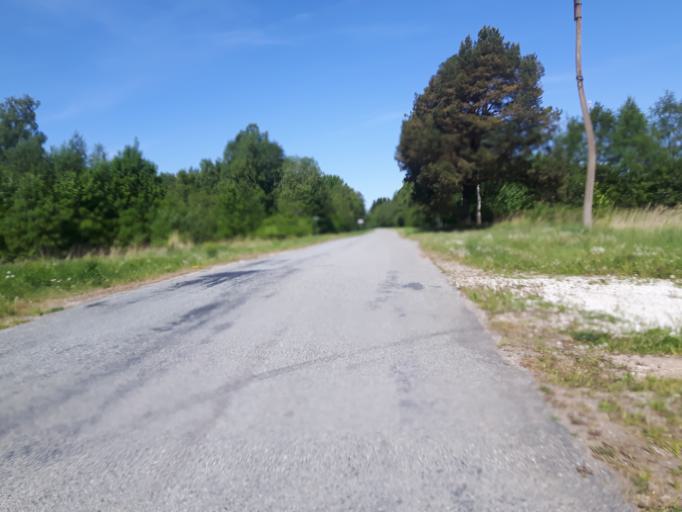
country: EE
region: Ida-Virumaa
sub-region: Aseri vald
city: Aseri
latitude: 59.4510
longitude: 26.8559
